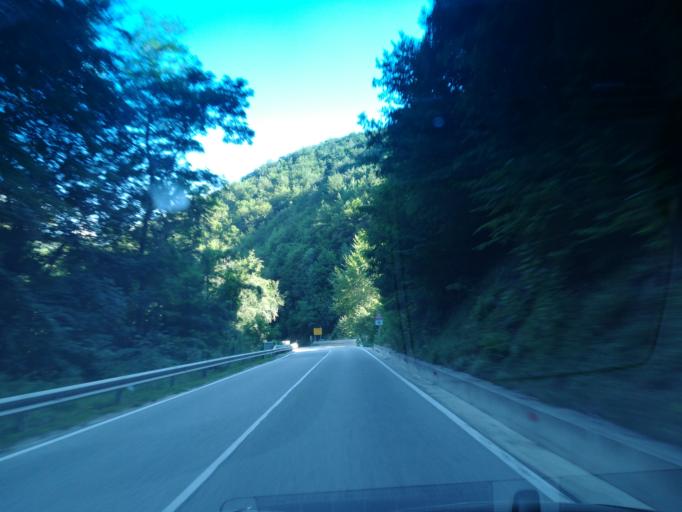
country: BG
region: Smolyan
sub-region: Obshtina Chepelare
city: Chepelare
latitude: 41.8062
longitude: 24.7088
